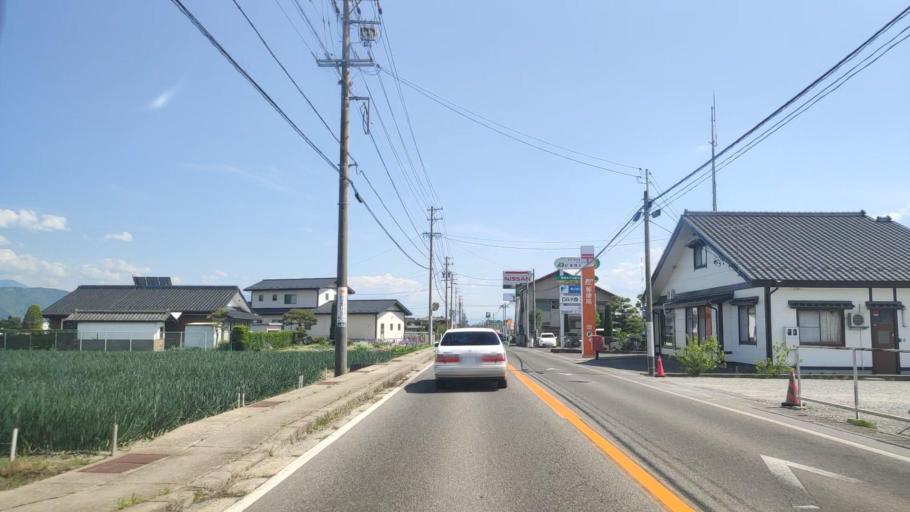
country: JP
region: Nagano
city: Hotaka
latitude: 36.3645
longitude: 137.8771
